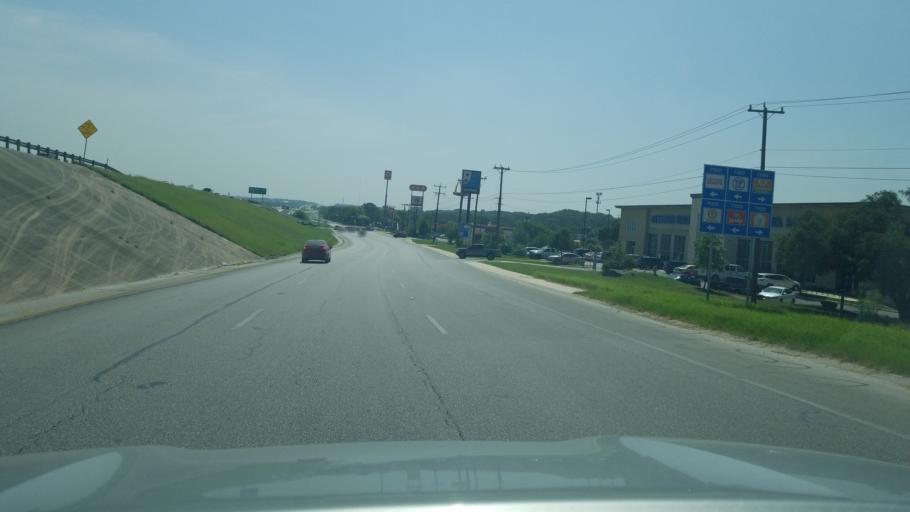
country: US
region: Texas
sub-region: Bexar County
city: Hollywood Park
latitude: 29.6001
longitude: -98.4217
